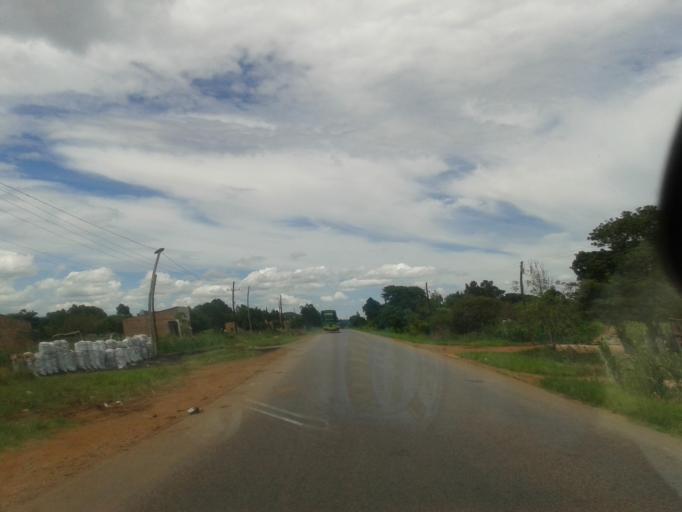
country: UG
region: Western Region
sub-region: Kiryandongo District
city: Masindi Port
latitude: 1.5180
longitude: 32.0589
